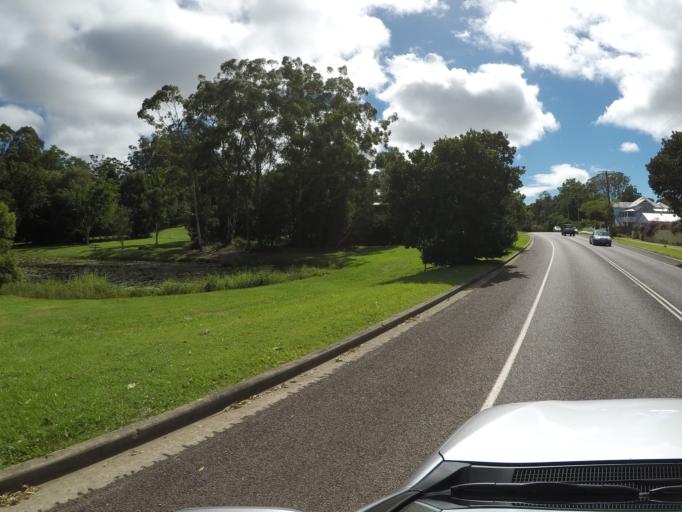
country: AU
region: Queensland
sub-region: Sunshine Coast
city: Nambour
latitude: -26.6268
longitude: 152.8624
